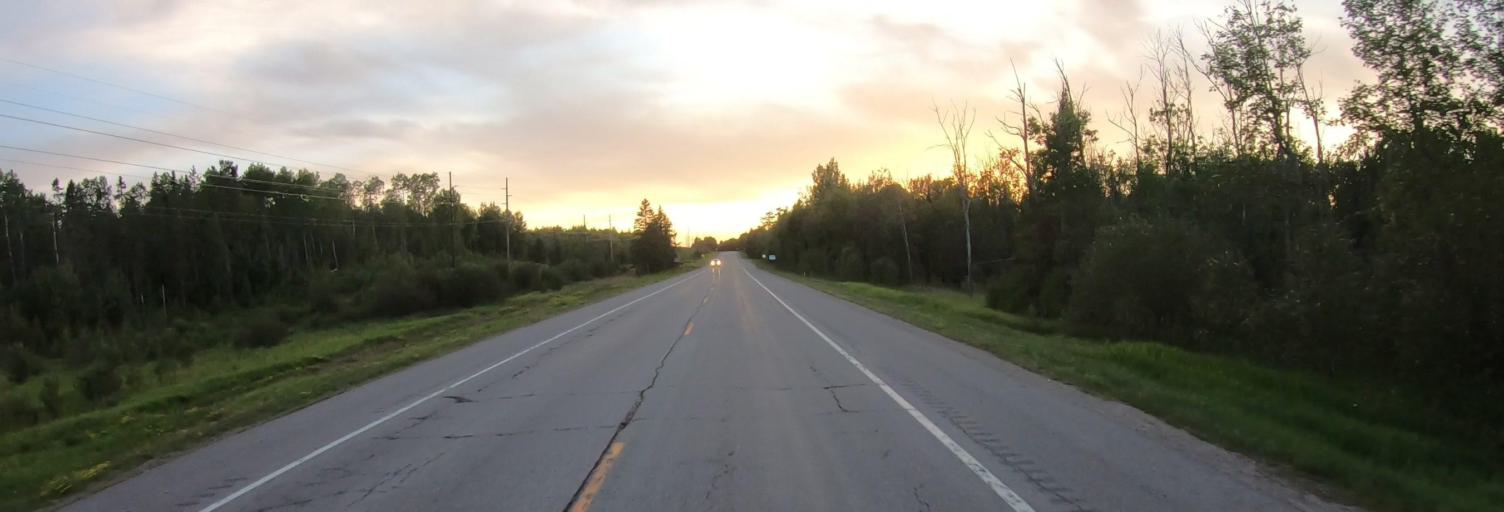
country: US
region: Minnesota
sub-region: Saint Louis County
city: Aurora
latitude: 47.7972
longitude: -92.3202
